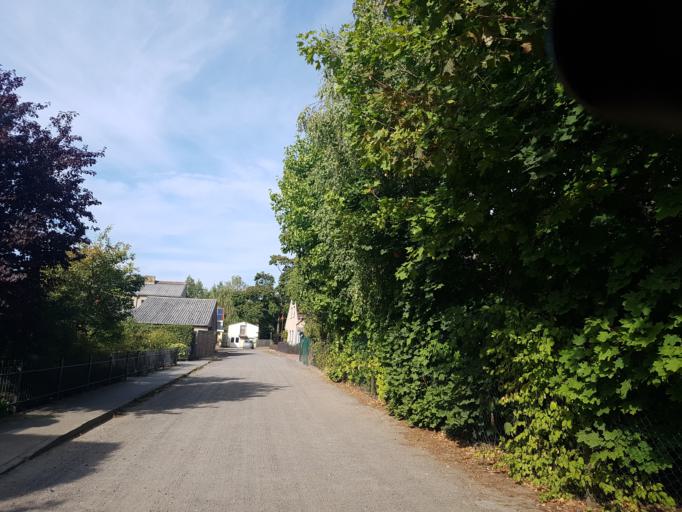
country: DE
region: Brandenburg
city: Wiesenburg
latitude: 52.1173
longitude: 12.4562
